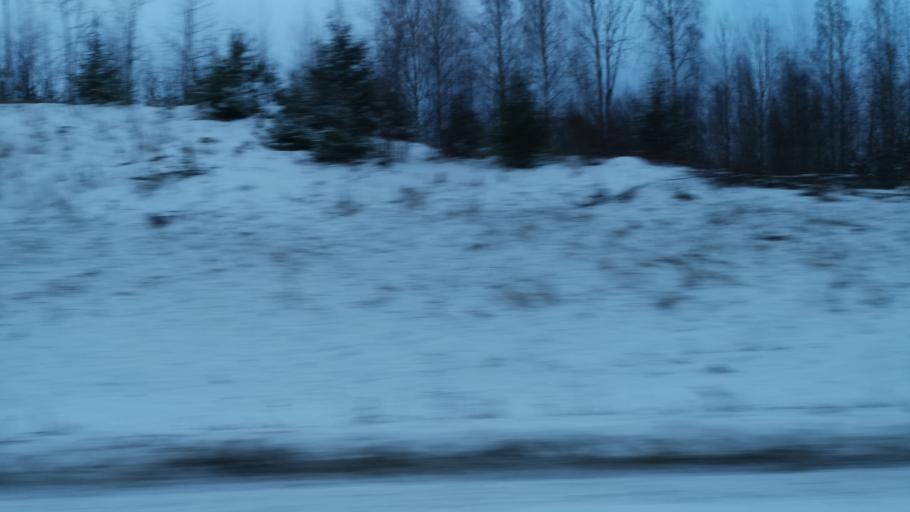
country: FI
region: Southern Savonia
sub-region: Savonlinna
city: Enonkoski
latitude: 62.1083
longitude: 28.6245
